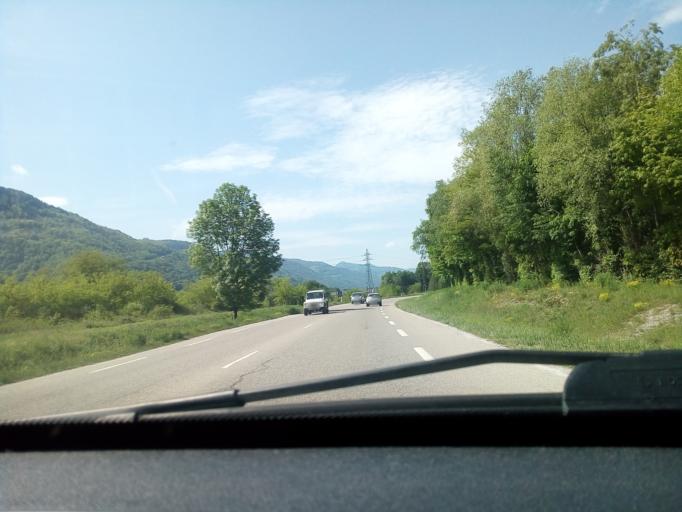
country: FR
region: Rhone-Alpes
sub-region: Departement de l'Isere
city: Froges
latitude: 45.2689
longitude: 5.9119
